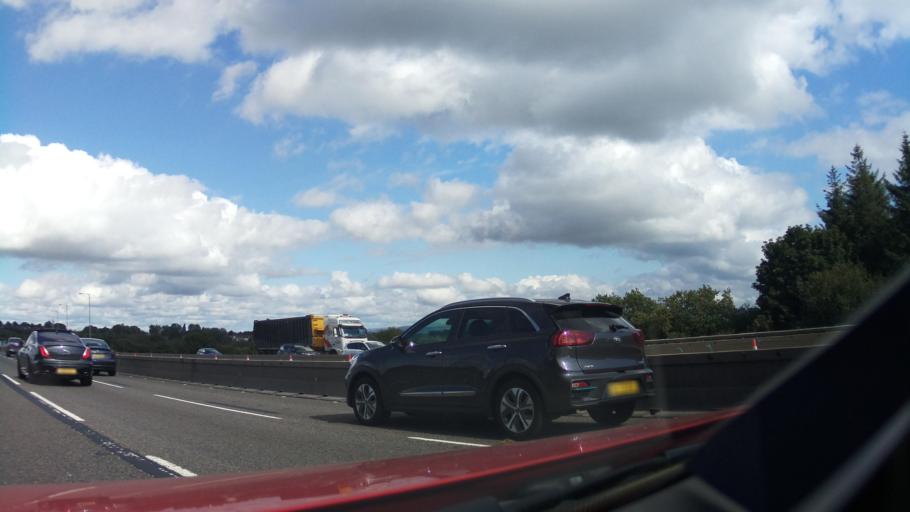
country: GB
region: England
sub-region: St. Helens
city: Billinge
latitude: 53.5265
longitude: -2.6983
